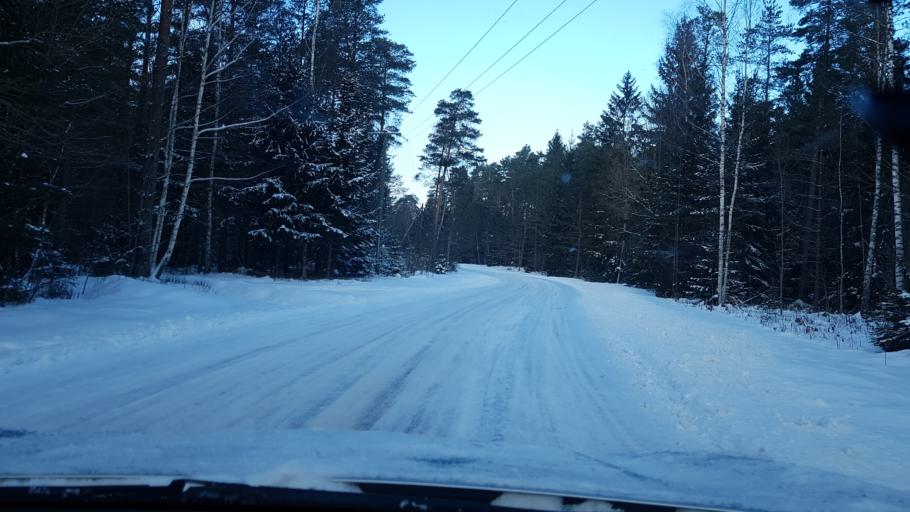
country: EE
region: Harju
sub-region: Nissi vald
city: Turba
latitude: 59.2162
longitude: 24.1404
